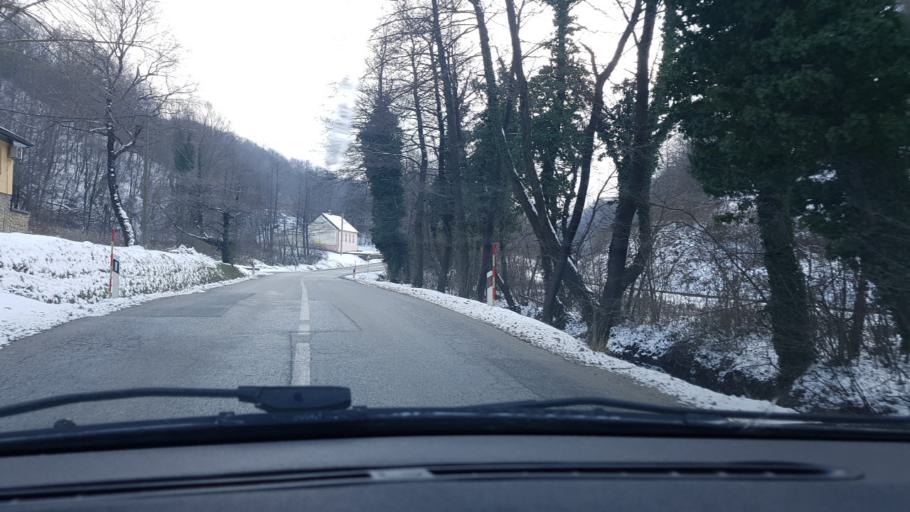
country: HR
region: Krapinsko-Zagorska
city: Mihovljan
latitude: 46.1831
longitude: 15.9842
